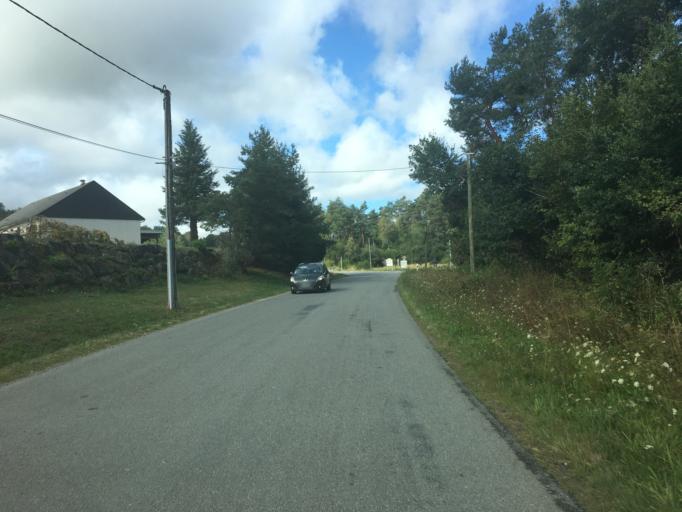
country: FR
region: Limousin
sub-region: Departement de la Correze
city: Bort-les-Orgues
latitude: 45.4202
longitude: 2.4538
